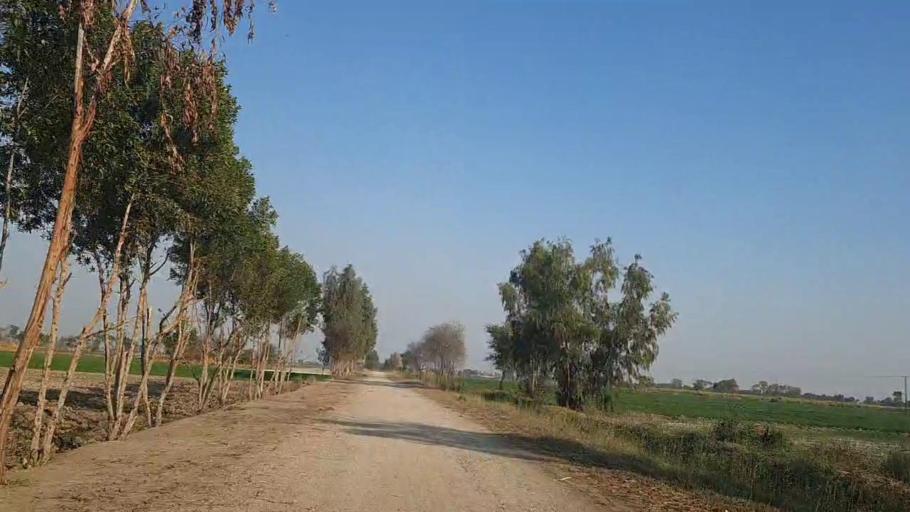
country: PK
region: Sindh
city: Daur
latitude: 26.3401
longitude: 68.1466
